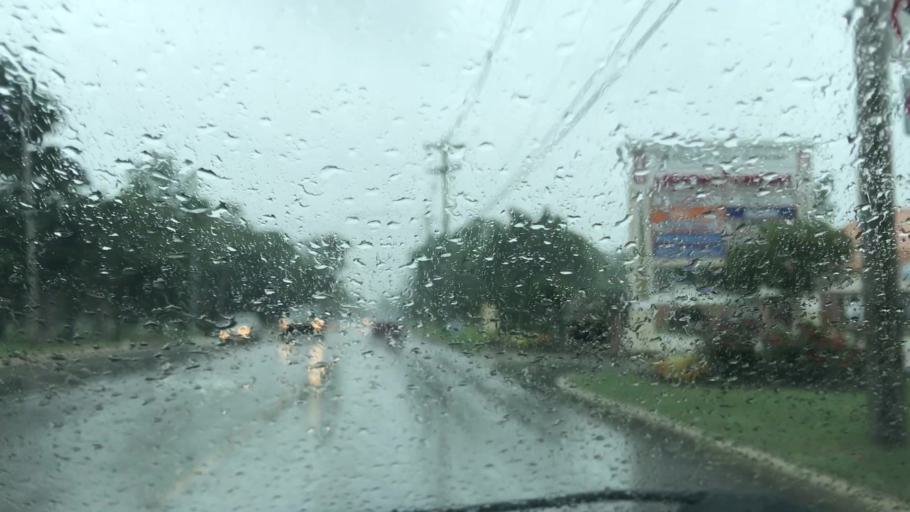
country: US
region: Indiana
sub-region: Boone County
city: Lebanon
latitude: 40.0608
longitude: -86.4716
